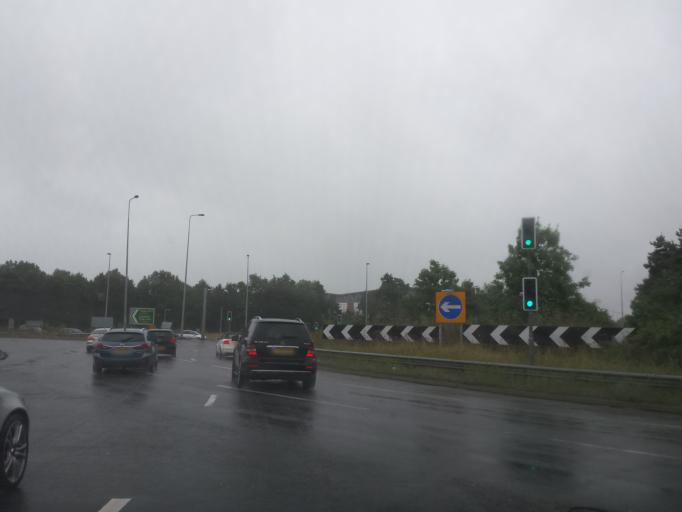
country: GB
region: England
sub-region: Leicestershire
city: Enderby
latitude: 52.6011
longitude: -1.1944
